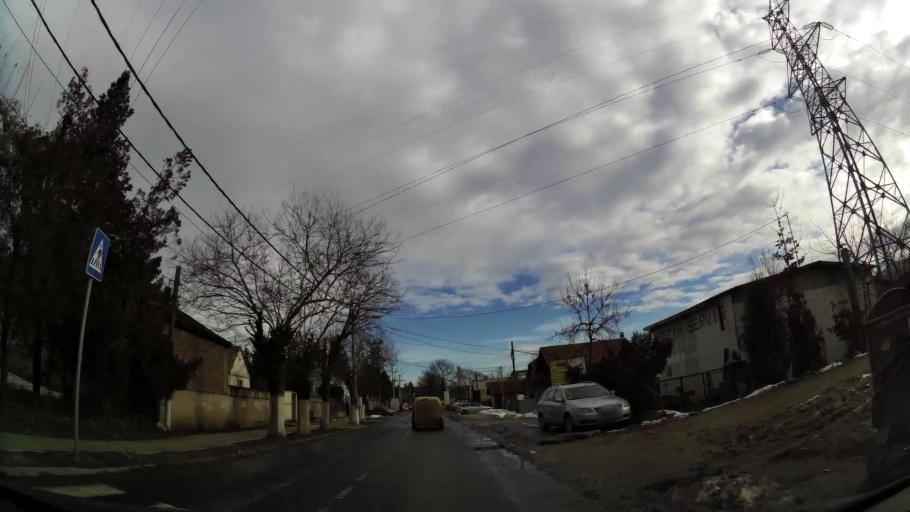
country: RS
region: Central Serbia
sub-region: Belgrade
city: Zemun
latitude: 44.8018
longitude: 20.3610
